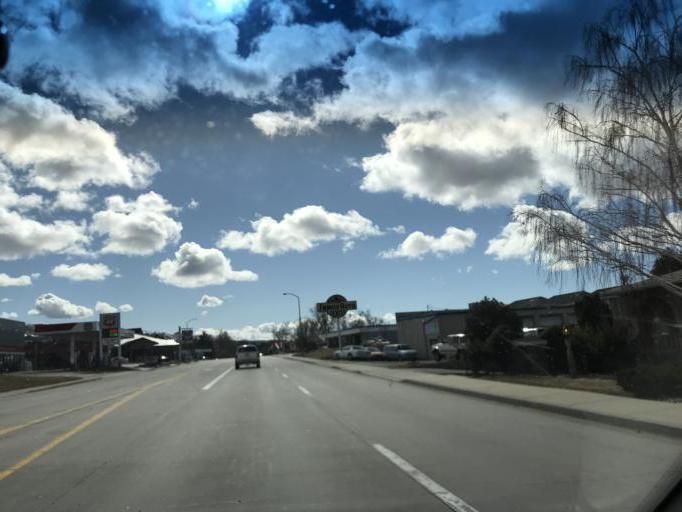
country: US
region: Utah
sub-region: Davis County
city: Woods Cross
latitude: 40.8688
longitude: -111.8777
